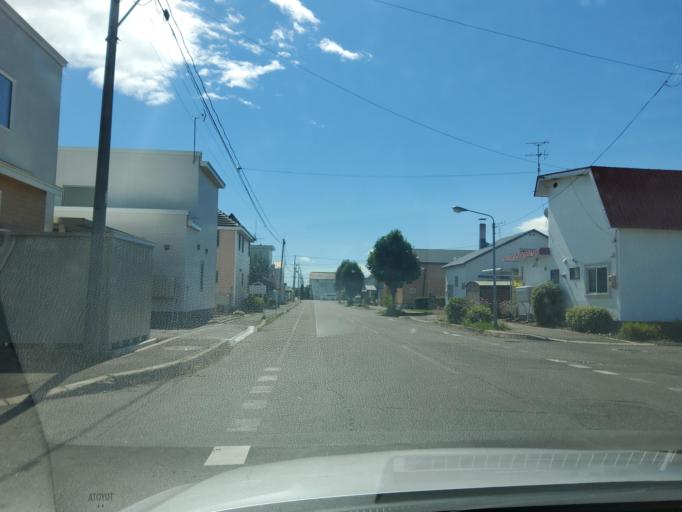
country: JP
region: Hokkaido
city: Otofuke
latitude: 42.9578
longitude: 143.1938
